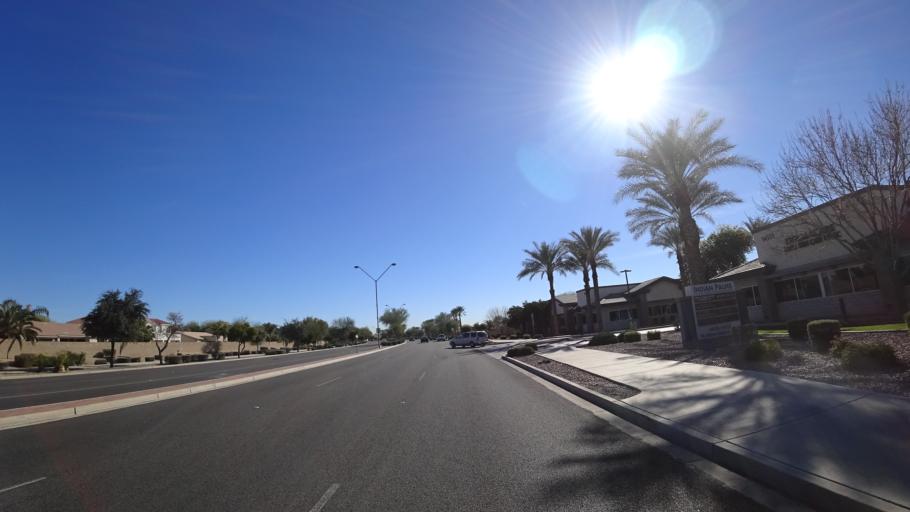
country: US
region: Arizona
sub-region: Maricopa County
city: Litchfield Park
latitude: 33.4865
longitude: -112.3729
